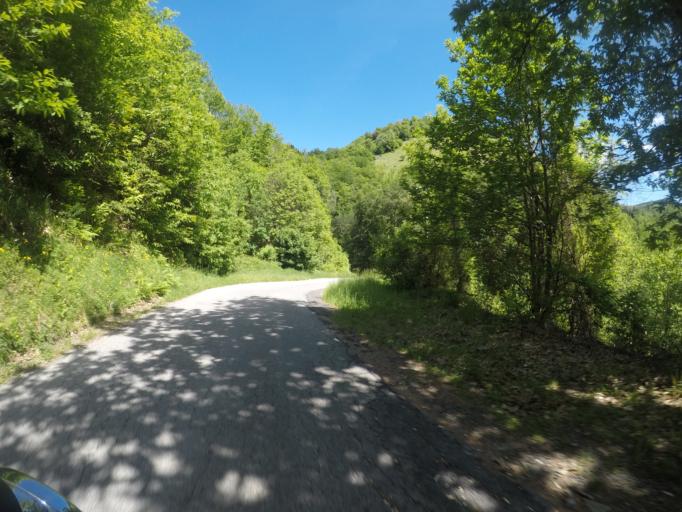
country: IT
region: Tuscany
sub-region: Provincia di Lucca
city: Careggine
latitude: 44.0944
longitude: 10.3245
